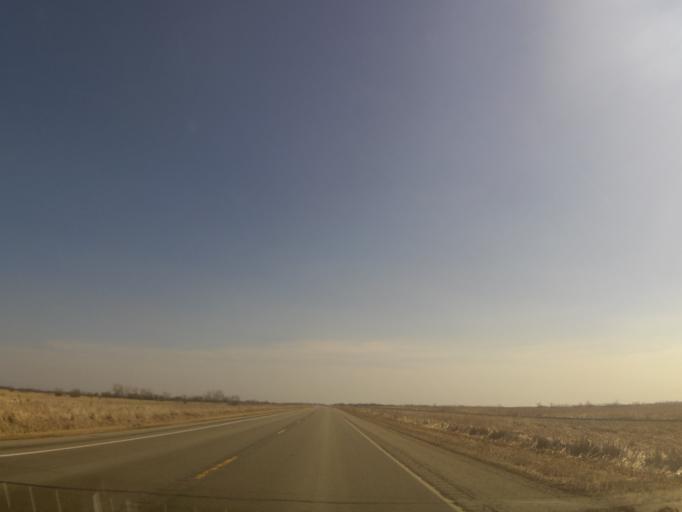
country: US
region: North Dakota
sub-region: Grand Forks County
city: Grand Forks Air Force Base
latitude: 48.1468
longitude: -97.2653
